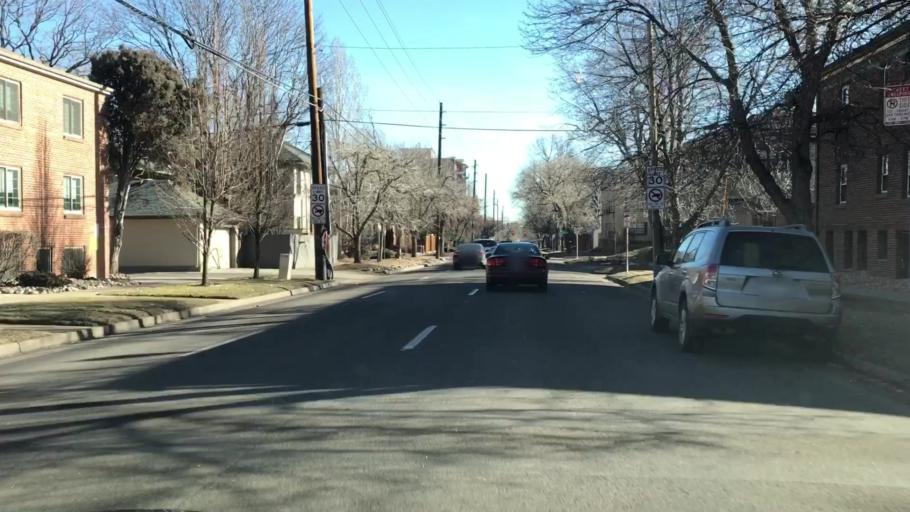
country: US
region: Colorado
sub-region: Denver County
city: Denver
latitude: 39.7384
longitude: -104.9516
